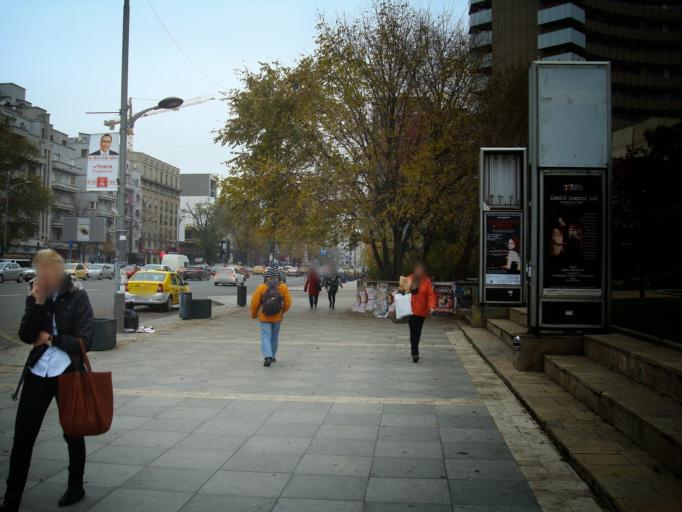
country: RO
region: Bucuresti
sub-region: Municipiul Bucuresti
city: Bucharest
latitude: 44.4361
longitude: 26.1025
